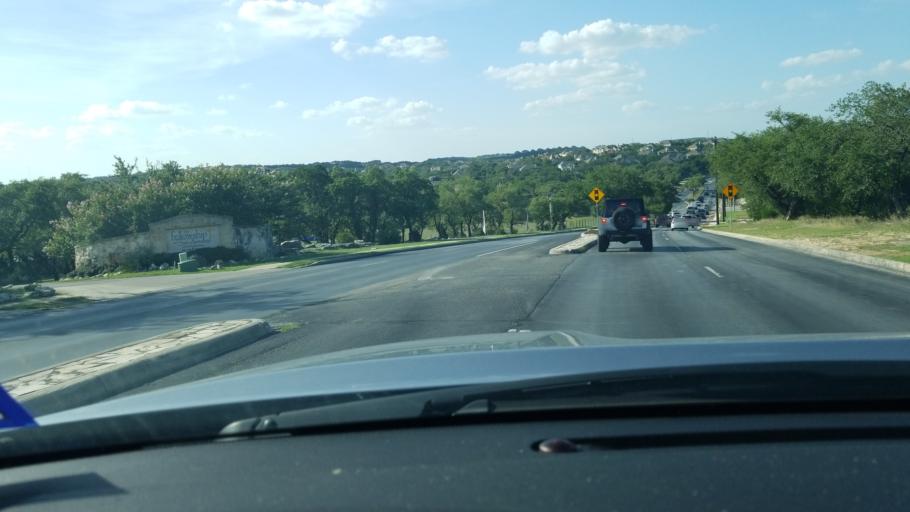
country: US
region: Texas
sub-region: Bexar County
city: Timberwood Park
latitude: 29.6643
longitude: -98.4783
